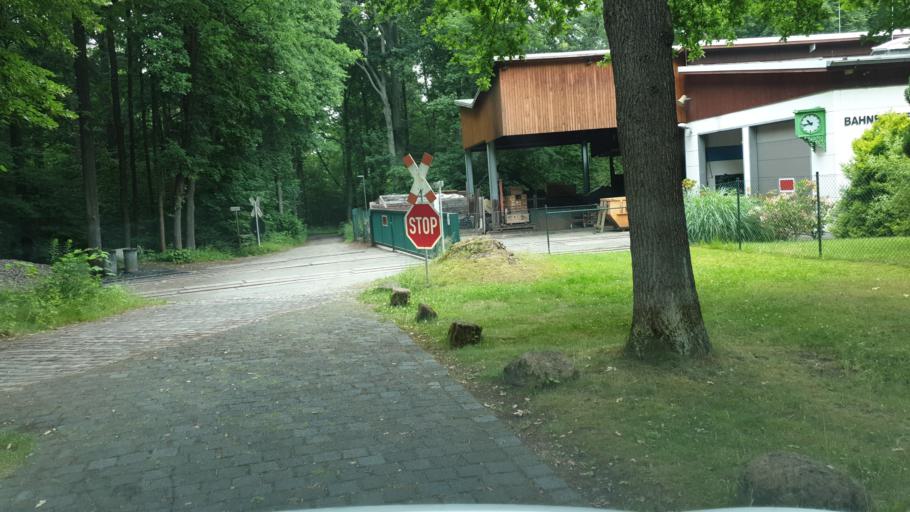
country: DE
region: Saxony
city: Chemnitz
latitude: 50.8499
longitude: 12.9144
